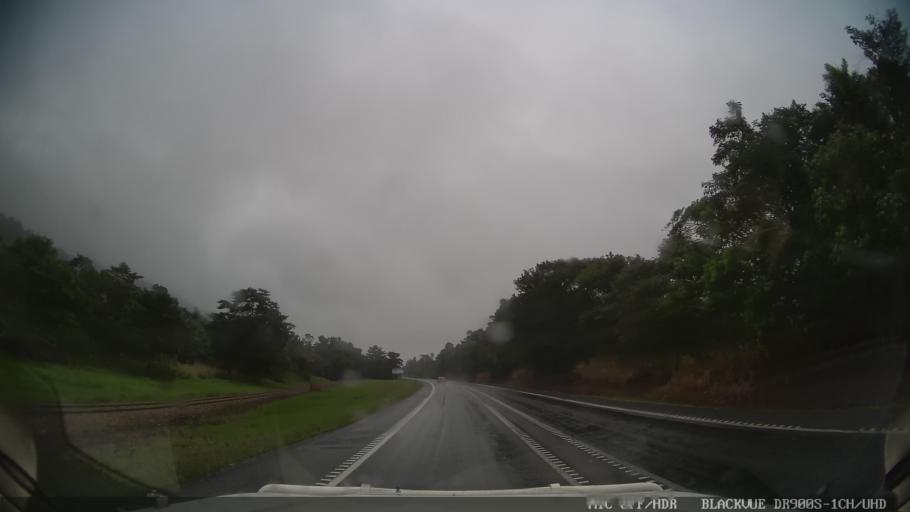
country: AU
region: Queensland
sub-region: Cassowary Coast
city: Innisfail
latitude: -17.8592
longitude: 145.9866
